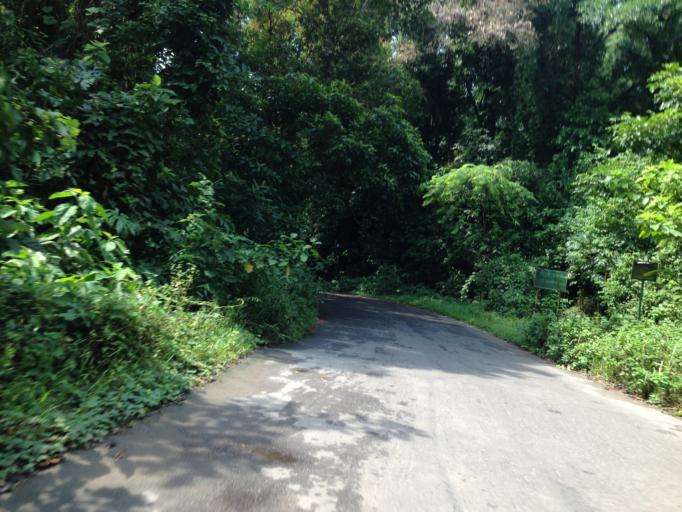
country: IN
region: Tripura
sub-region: Dhalai
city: Kamalpur
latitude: 24.3167
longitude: 91.7768
